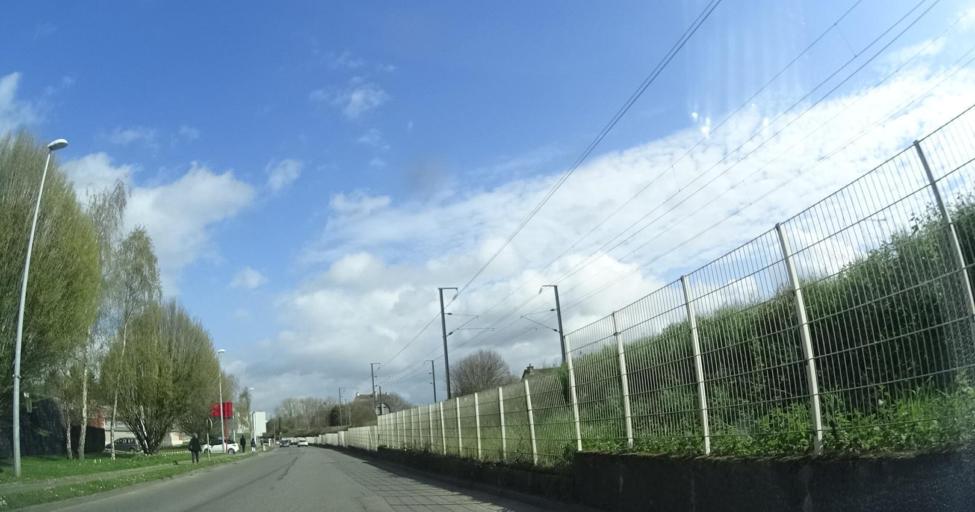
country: FR
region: Brittany
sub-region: Departement d'Ille-et-Vilaine
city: Rennes
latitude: 48.1210
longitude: -1.6894
